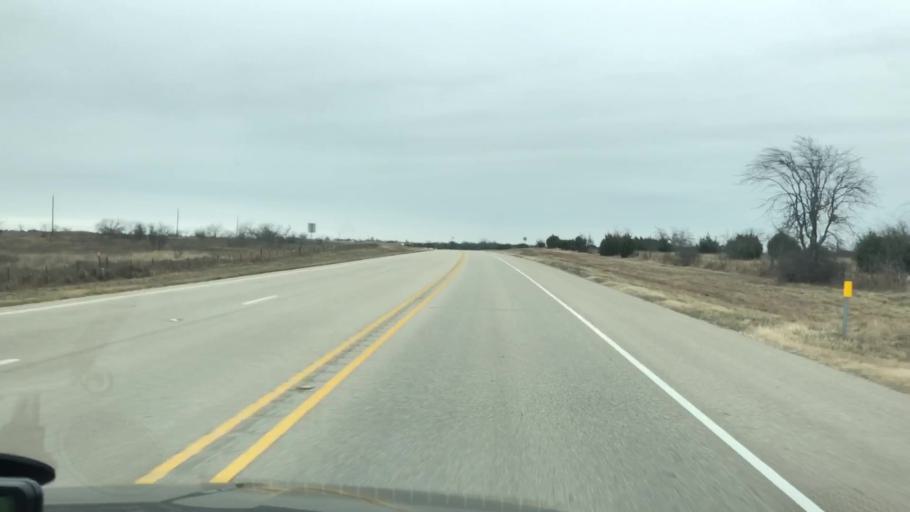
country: US
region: Texas
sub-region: Hamilton County
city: Hamilton
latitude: 31.8501
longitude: -98.1120
